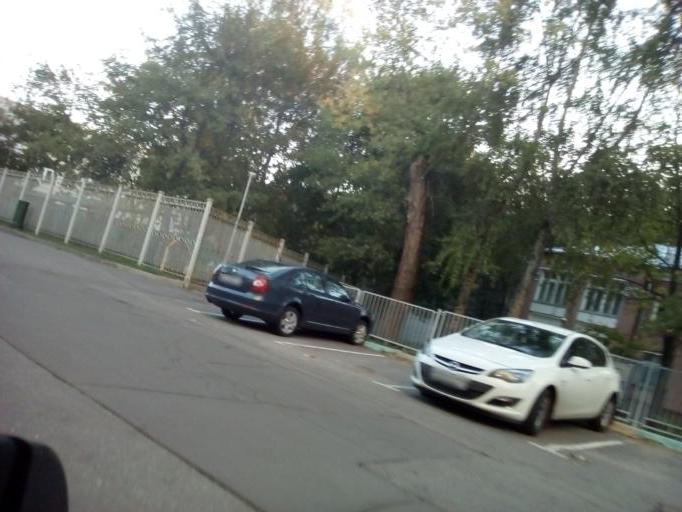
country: RU
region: Moskovskaya
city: Koptevo
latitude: 55.8185
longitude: 37.4906
